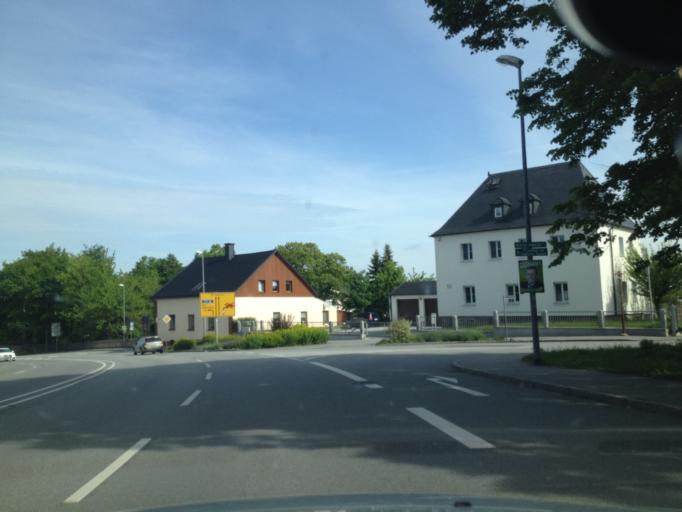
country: DE
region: Saxony
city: Annaberg-Buchholz
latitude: 50.5885
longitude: 13.0156
